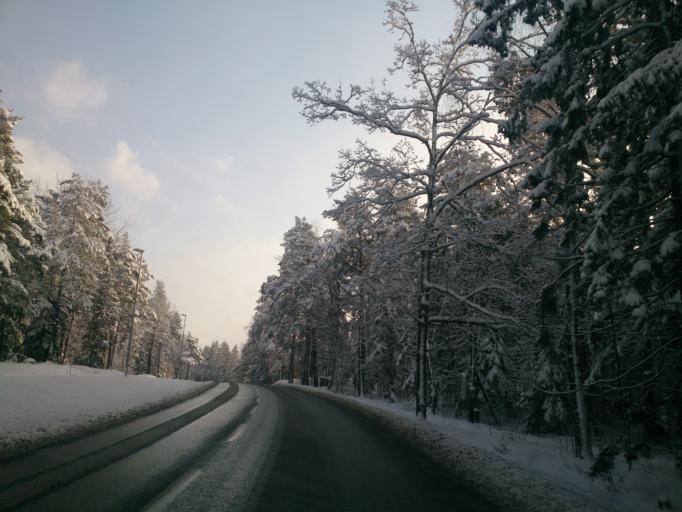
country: SE
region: Stockholm
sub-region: Varmdo Kommun
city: Hemmesta
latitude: 59.2889
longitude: 18.5263
